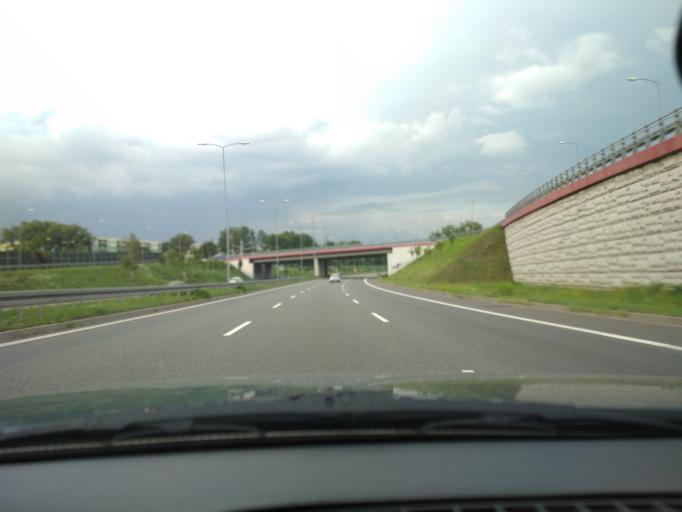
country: PL
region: Silesian Voivodeship
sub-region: Ruda Slaska
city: Ruda Slaska
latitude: 50.2961
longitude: 18.8303
